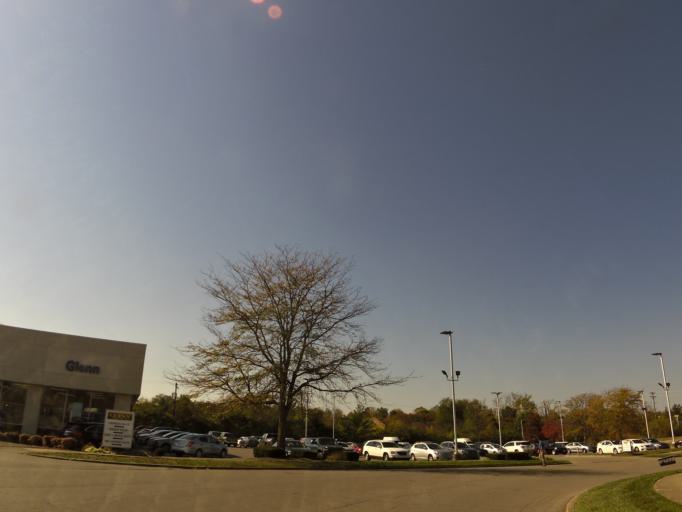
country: US
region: Kentucky
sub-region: Fayette County
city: Lexington
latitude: 37.9979
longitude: -84.4430
